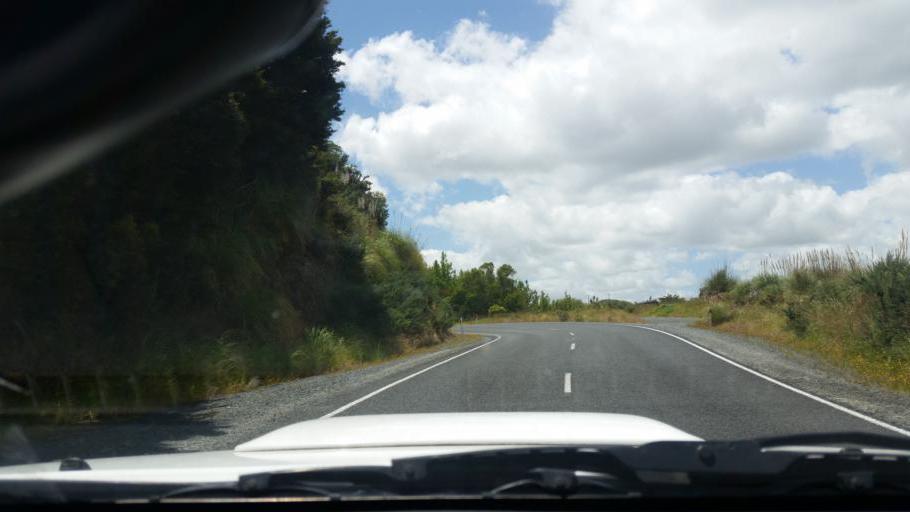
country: NZ
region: Northland
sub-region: Whangarei
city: Ruakaka
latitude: -36.0836
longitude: 174.2396
